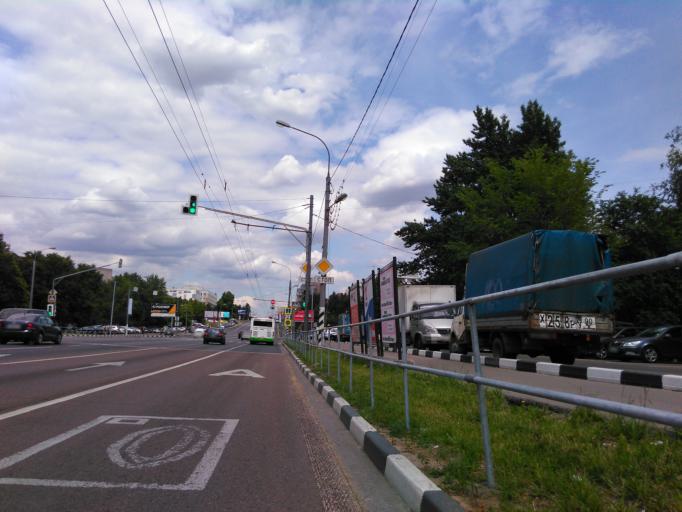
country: RU
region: Moscow
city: Zyuzino
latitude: 55.6652
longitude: 37.5805
